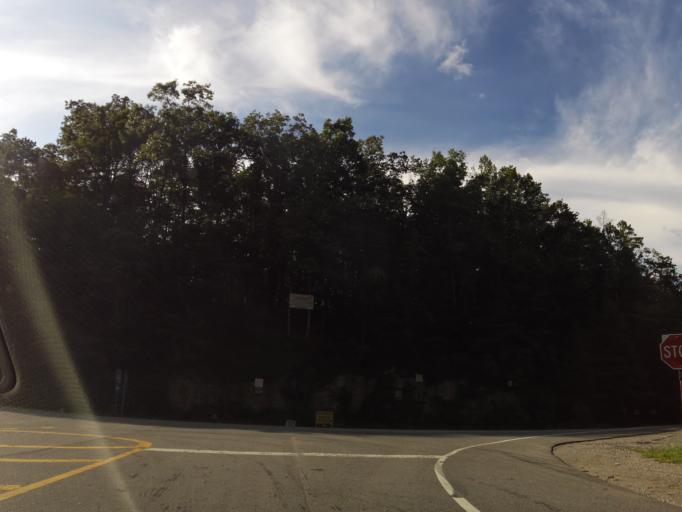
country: US
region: Tennessee
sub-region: Campbell County
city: Jacksboro
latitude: 36.4168
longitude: -84.2815
